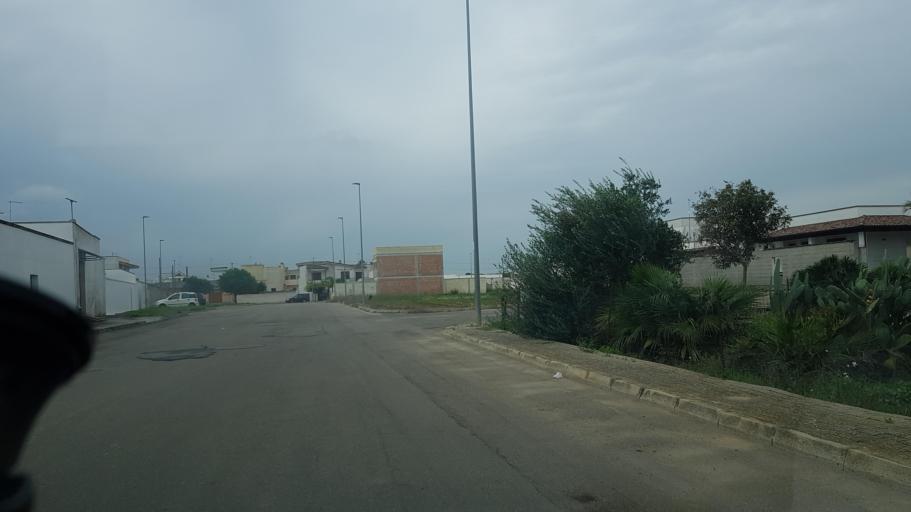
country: IT
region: Apulia
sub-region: Provincia di Lecce
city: Guagnano
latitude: 40.4058
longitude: 17.9520
